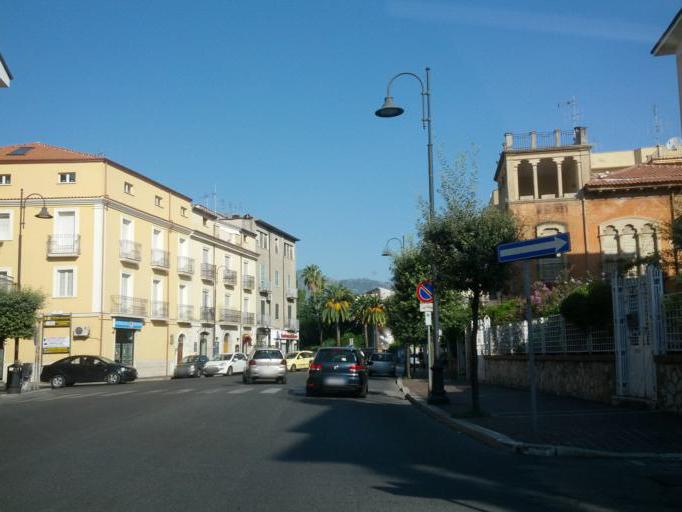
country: IT
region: Latium
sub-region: Provincia di Latina
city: Fondi
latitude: 41.3551
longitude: 13.4301
